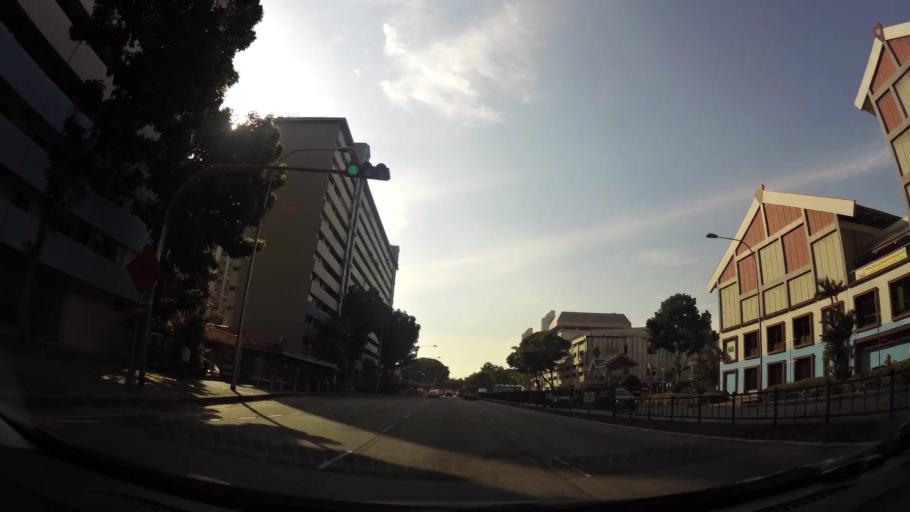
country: SG
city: Singapore
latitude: 1.3223
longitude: 103.8706
